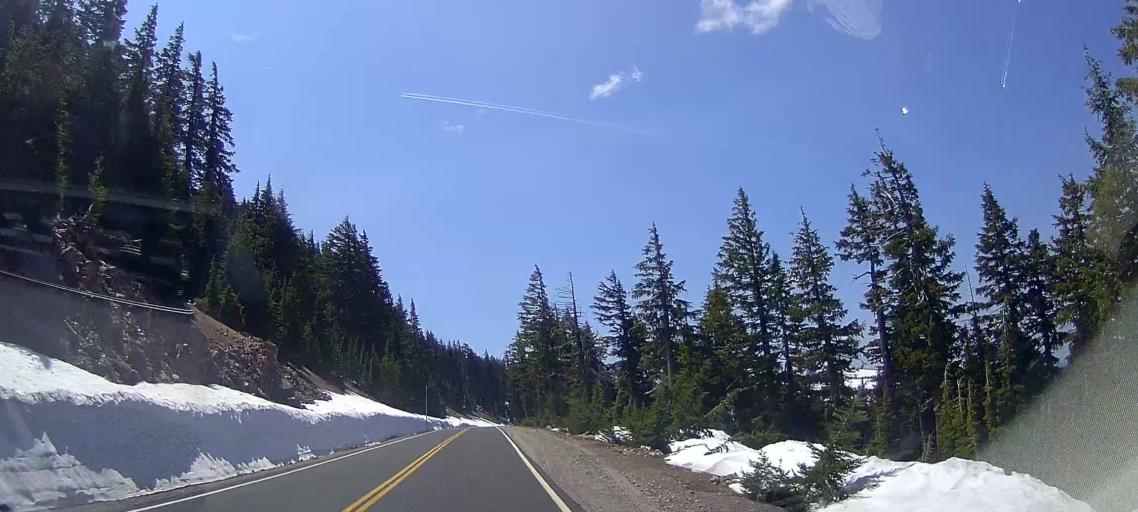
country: US
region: Oregon
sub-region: Jackson County
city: Shady Cove
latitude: 42.9758
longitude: -122.1430
